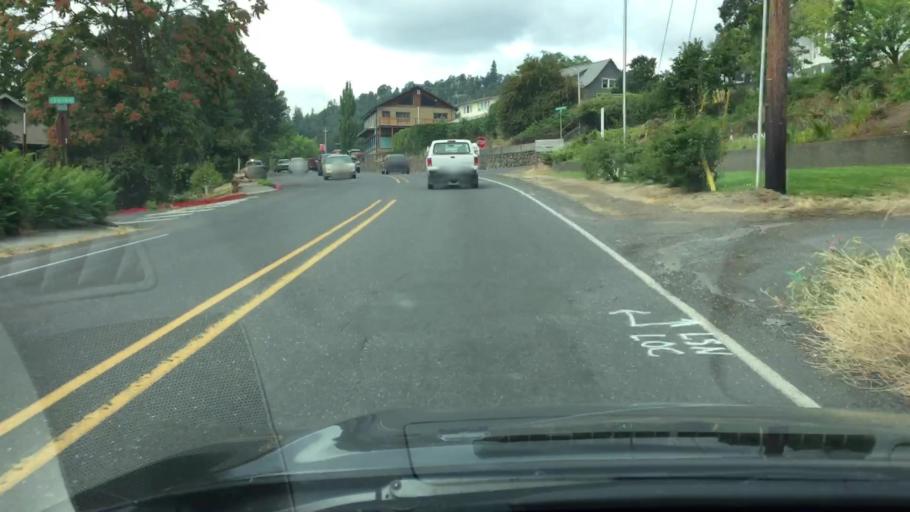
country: US
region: Washington
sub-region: Klickitat County
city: White Salmon
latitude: 45.7264
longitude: -121.4812
